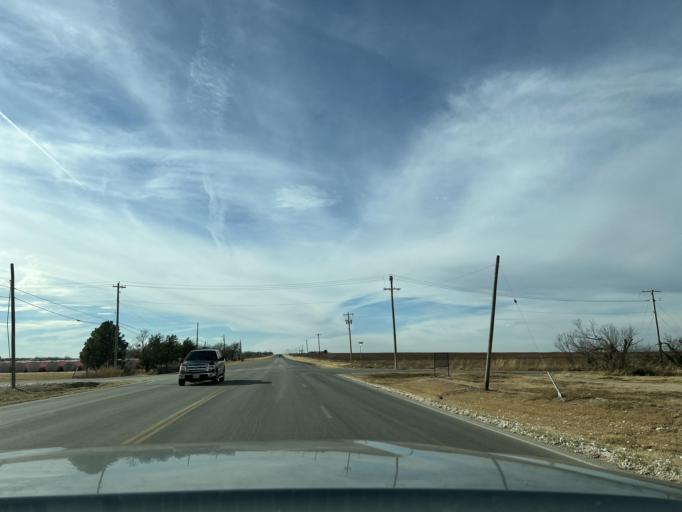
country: US
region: Texas
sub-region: Jones County
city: Anson
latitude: 32.7517
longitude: -99.9047
